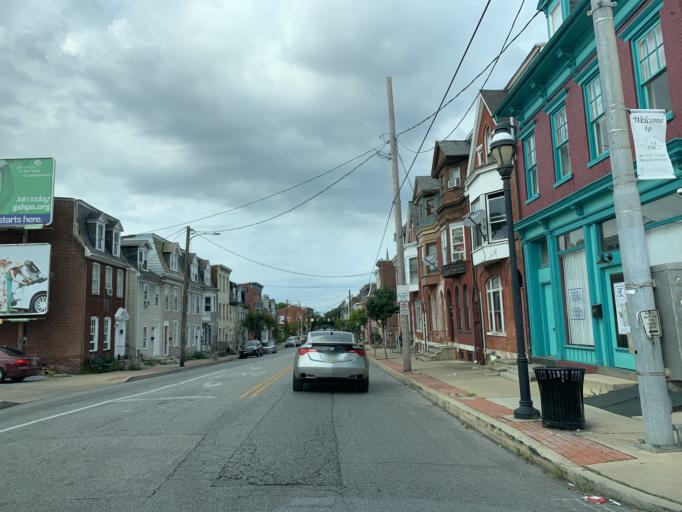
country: US
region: Pennsylvania
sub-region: York County
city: York
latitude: 39.9609
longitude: -76.7224
